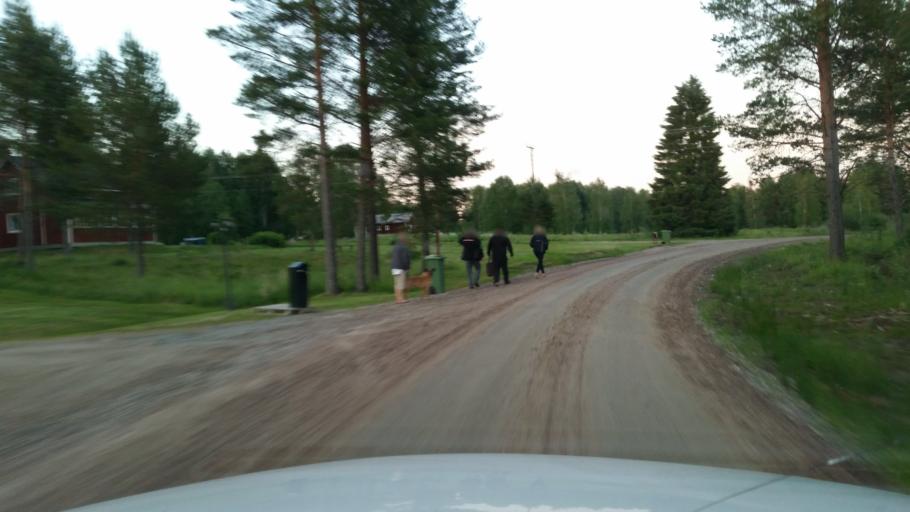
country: SE
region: Vaesternorrland
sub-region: Ange Kommun
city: Ange
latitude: 62.1846
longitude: 15.6356
